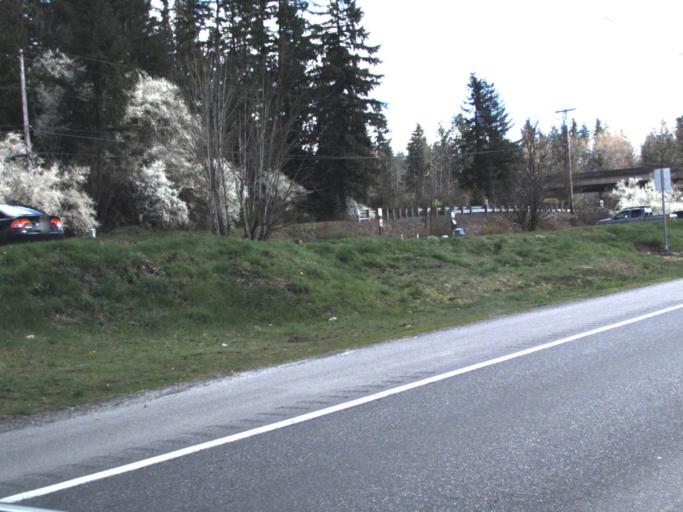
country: US
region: Washington
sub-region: King County
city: Maple Valley
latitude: 47.4101
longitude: -122.0392
